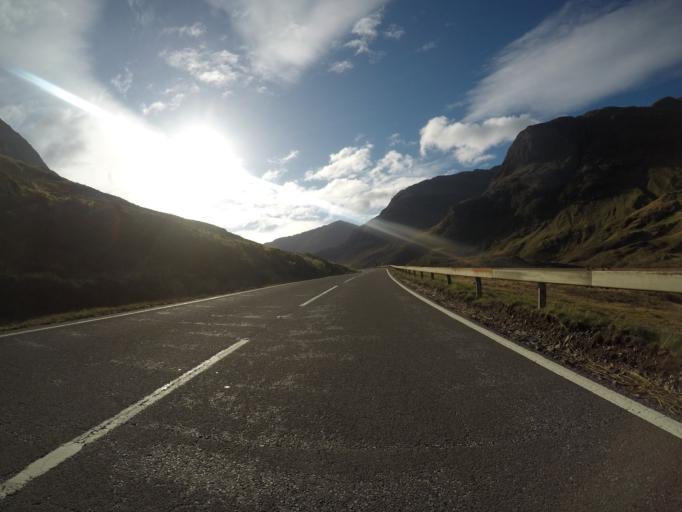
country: GB
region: Scotland
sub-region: Highland
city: Fort William
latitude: 56.6689
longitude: -4.9980
